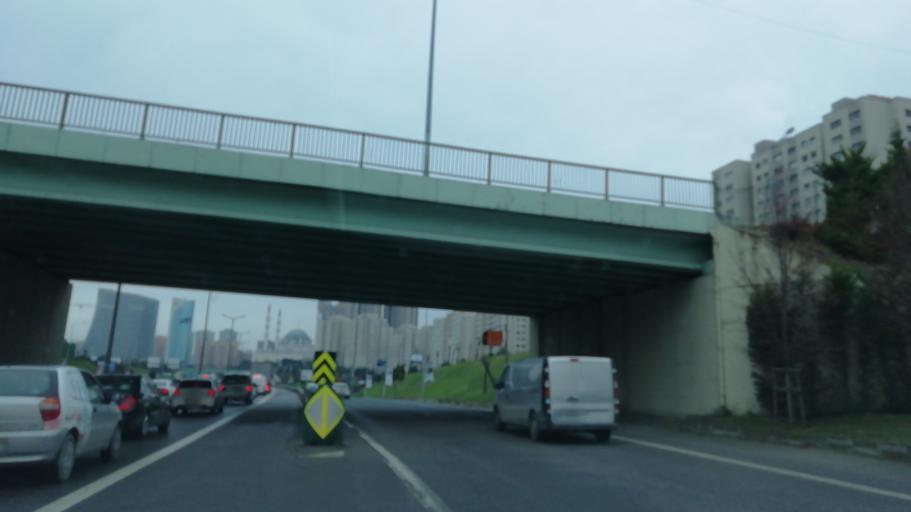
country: TR
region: Istanbul
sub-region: Atasehir
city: Atasehir
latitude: 41.0007
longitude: 29.1058
